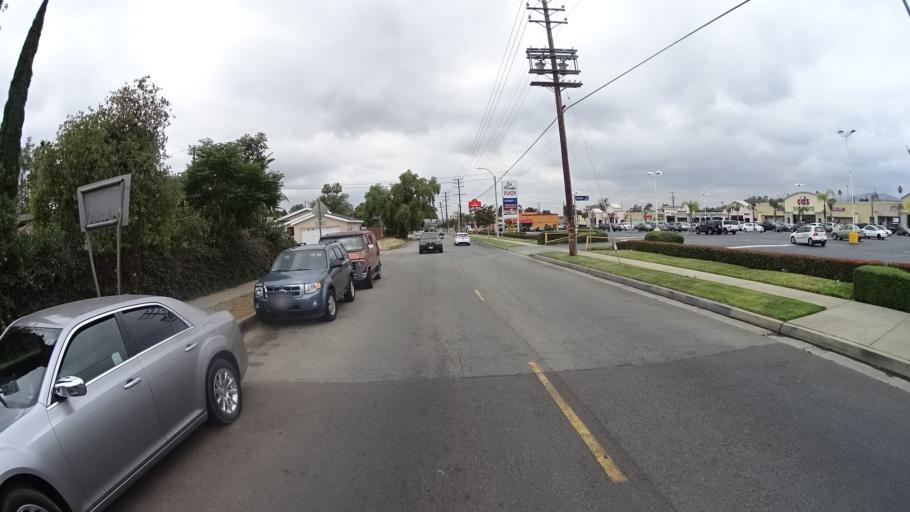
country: US
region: California
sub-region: Los Angeles County
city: San Fernando
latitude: 34.2814
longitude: -118.4524
